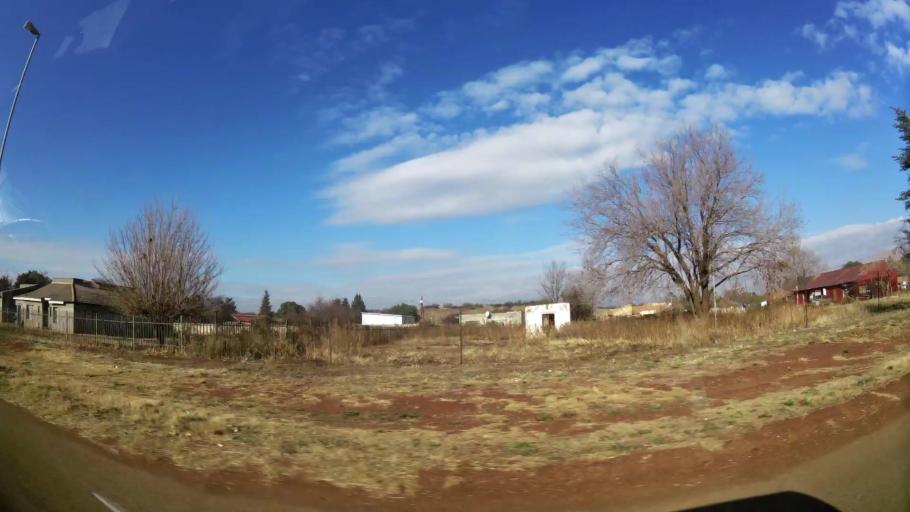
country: ZA
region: Gauteng
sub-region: Sedibeng District Municipality
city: Meyerton
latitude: -26.5035
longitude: 28.0664
